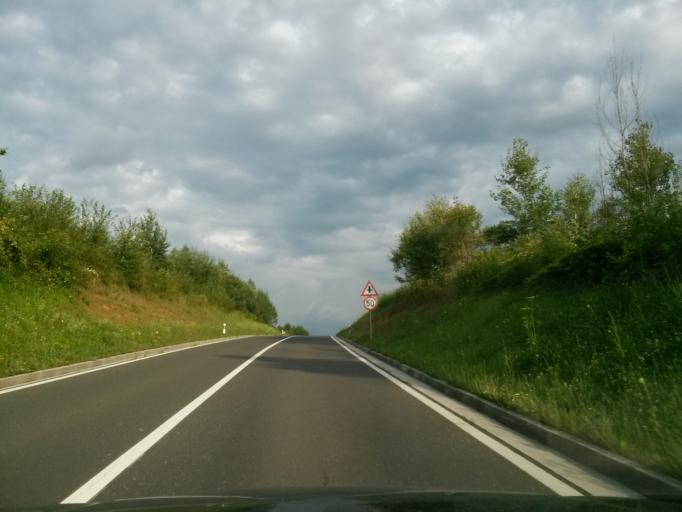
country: HR
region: Sisacko-Moslavacka
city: Gvozd
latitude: 45.3275
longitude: 15.9377
